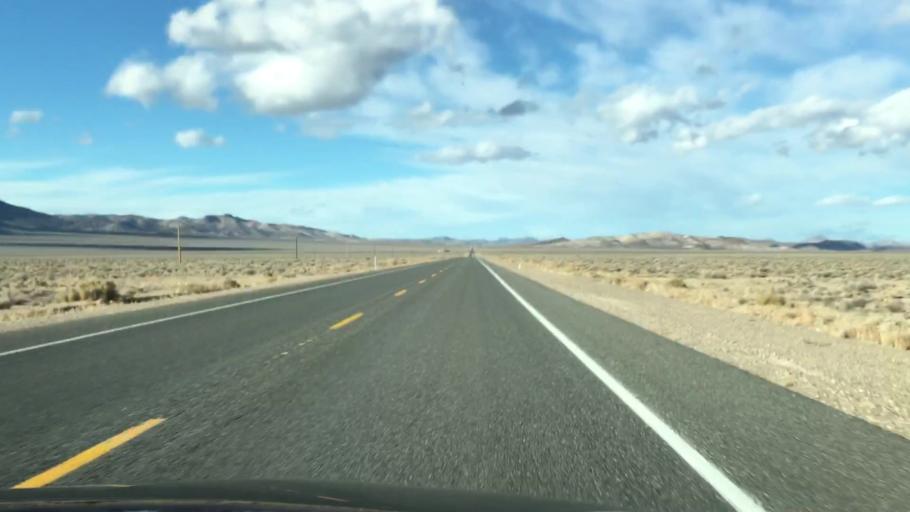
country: US
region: Nevada
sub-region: Esmeralda County
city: Goldfield
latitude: 37.4755
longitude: -117.1775
